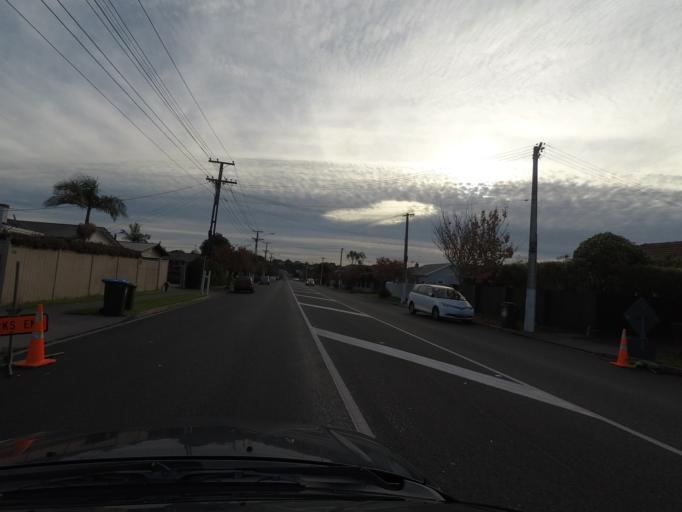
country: NZ
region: Auckland
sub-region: Auckland
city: Tamaki
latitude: -36.8910
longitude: 174.8206
